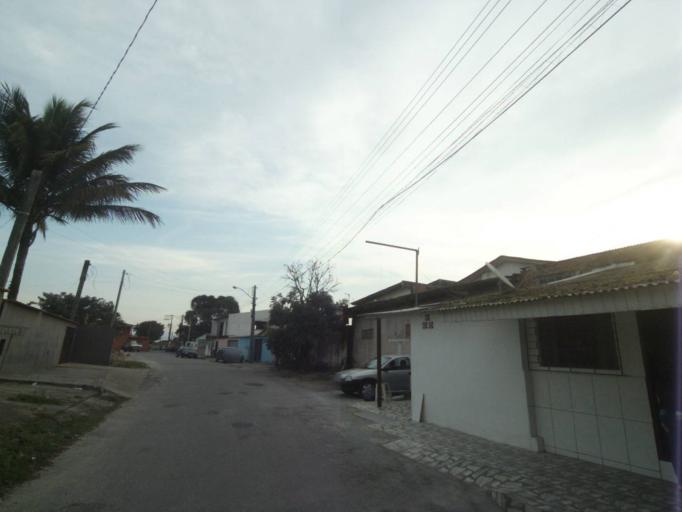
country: BR
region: Parana
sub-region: Paranagua
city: Paranagua
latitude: -25.5262
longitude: -48.5306
